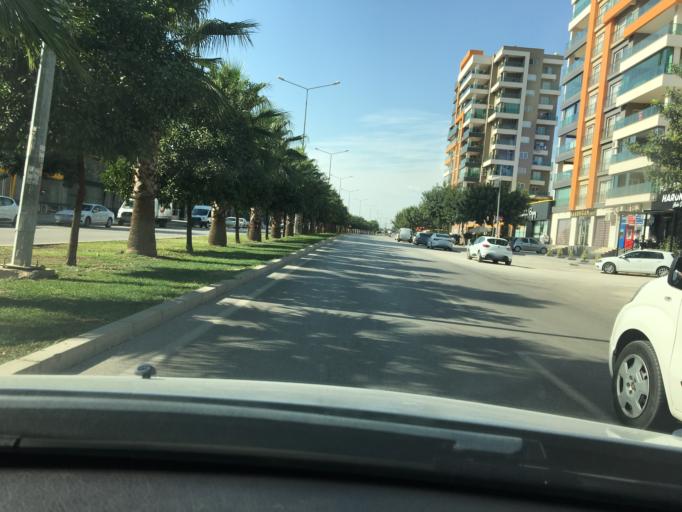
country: TR
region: Adana
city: Seyhan
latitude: 37.0227
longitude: 35.2572
